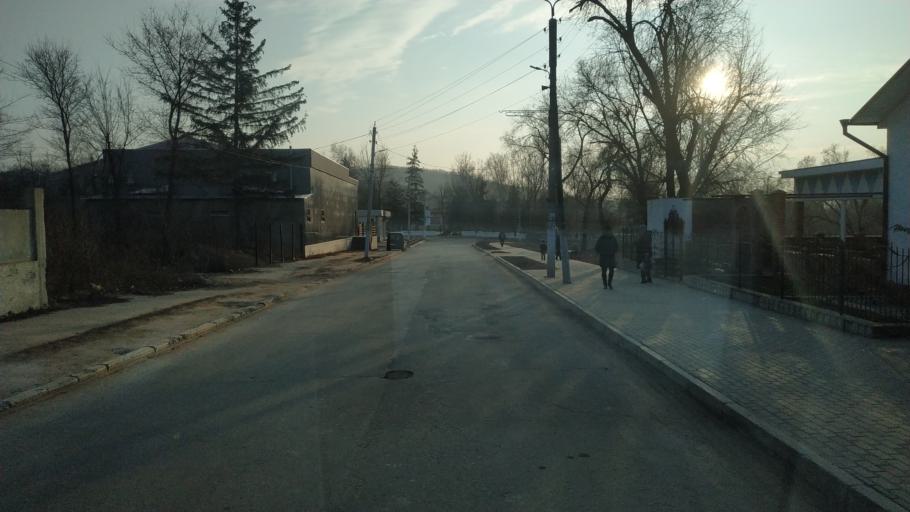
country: MD
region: Hincesti
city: Dancu
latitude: 46.7614
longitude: 28.3579
